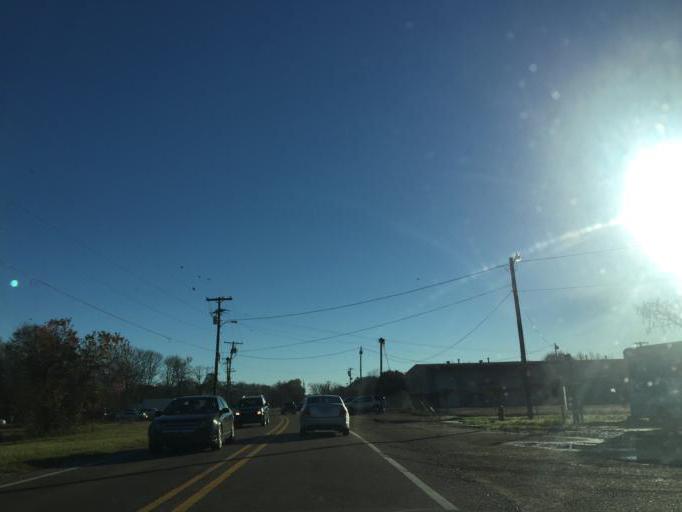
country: US
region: Mississippi
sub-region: Hinds County
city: Jackson
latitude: 32.2831
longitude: -90.1699
